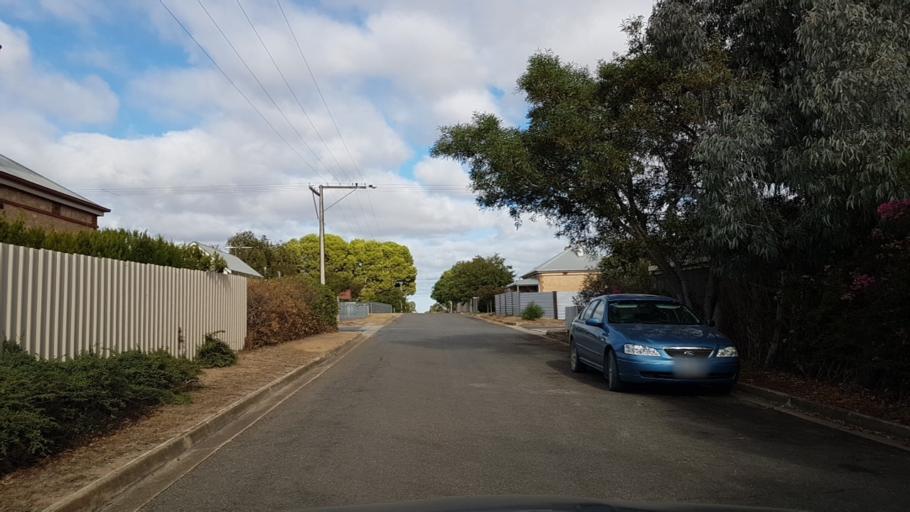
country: AU
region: South Australia
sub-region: Alexandrina
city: Langhorne Creek
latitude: -35.4045
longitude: 138.9716
